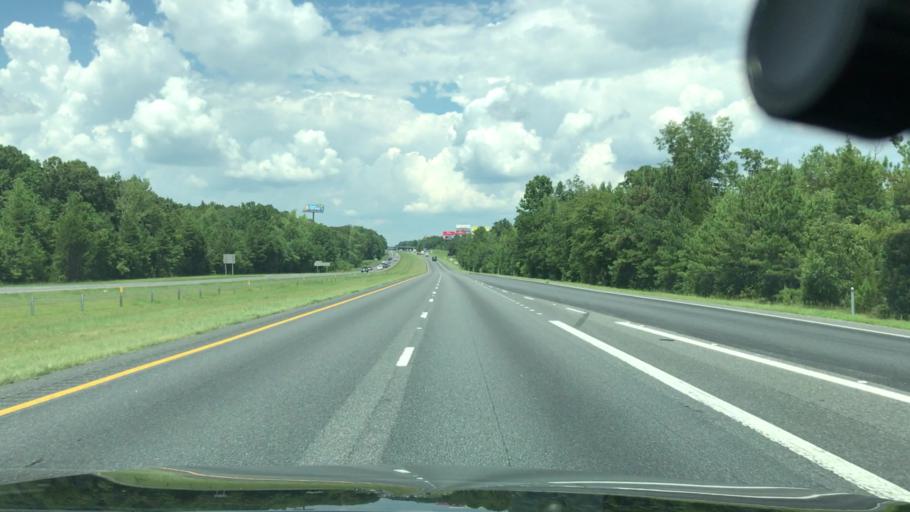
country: US
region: South Carolina
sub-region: York County
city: Lesslie
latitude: 34.8932
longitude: -80.9933
